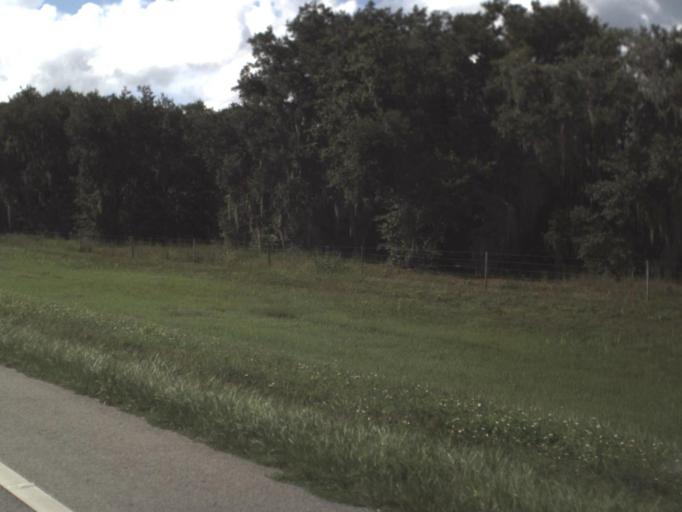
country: US
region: Florida
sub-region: Hillsborough County
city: Wimauma
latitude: 27.4736
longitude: -82.2142
